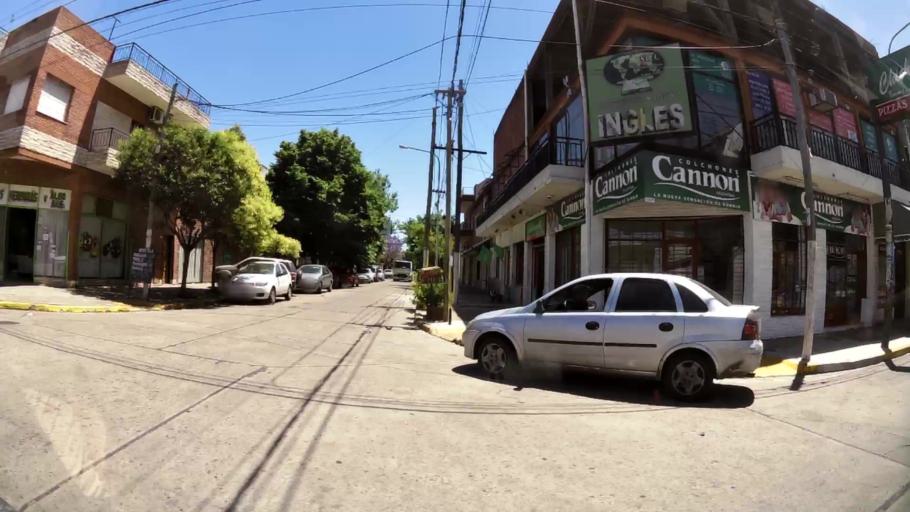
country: AR
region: Buenos Aires
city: Caseros
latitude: -34.5984
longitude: -58.5616
